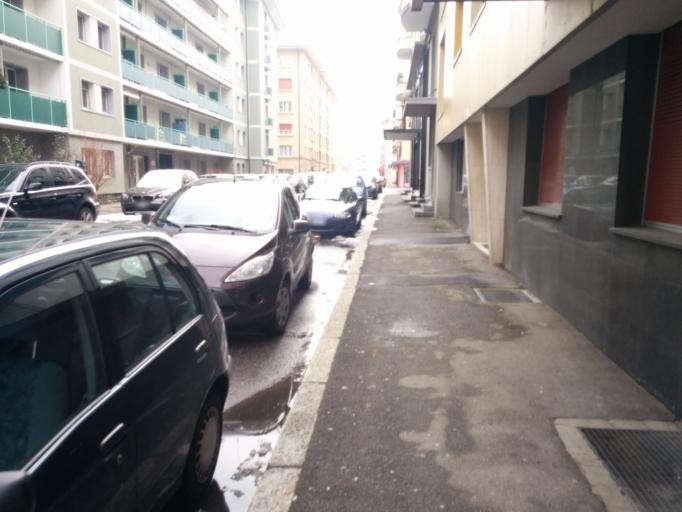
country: CH
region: Fribourg
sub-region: Sarine District
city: Fribourg
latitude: 46.7997
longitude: 7.1504
